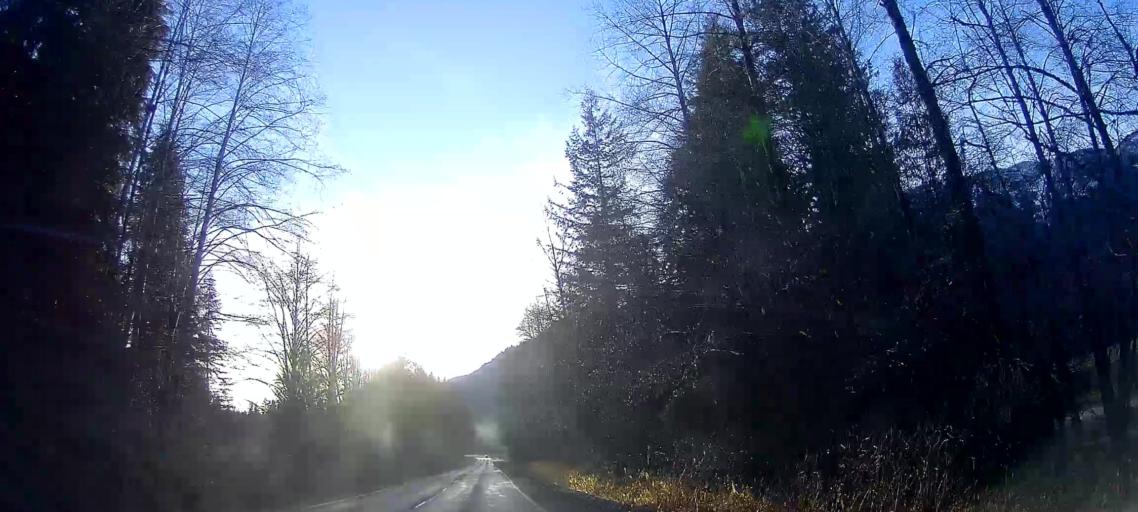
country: US
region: Washington
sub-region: Snohomish County
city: Darrington
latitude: 48.6041
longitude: -121.7608
